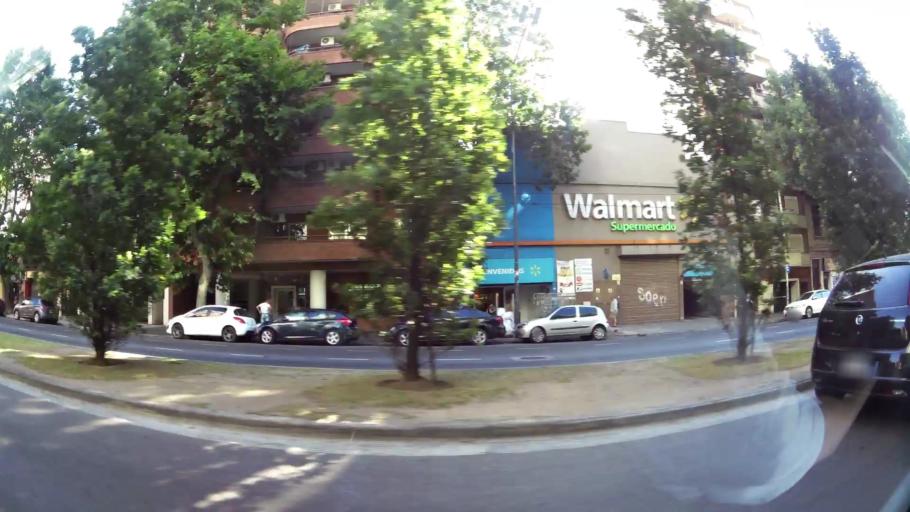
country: AR
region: Buenos Aires F.D.
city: Villa Santa Rita
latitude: -34.6124
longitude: -58.4418
